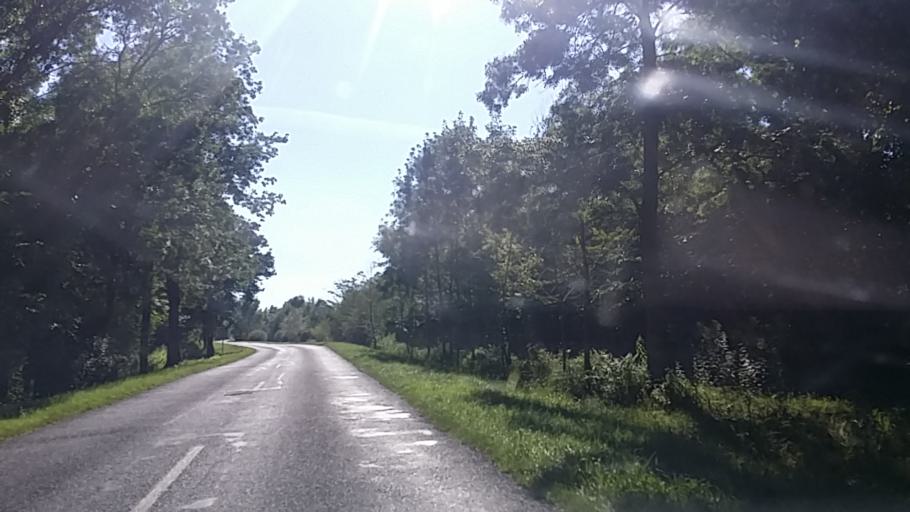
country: HU
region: Somogy
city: Balatonbereny
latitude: 46.7044
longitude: 17.2856
